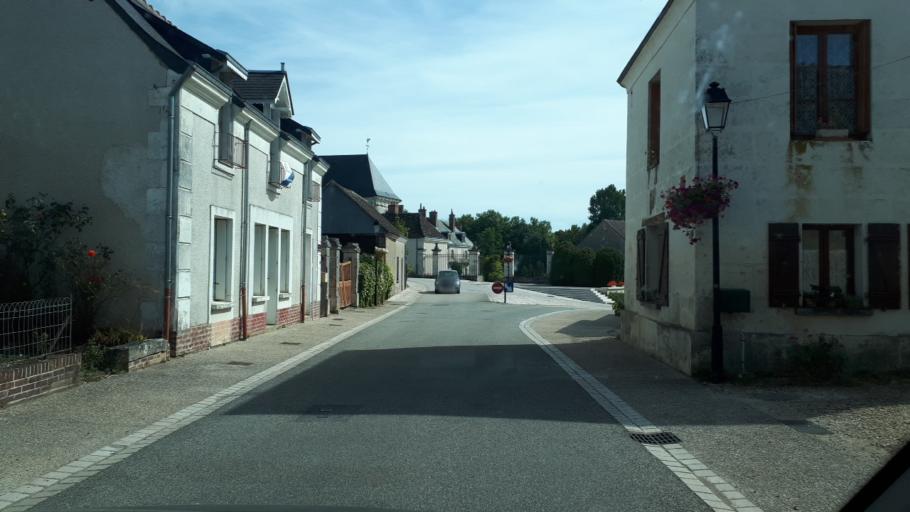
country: FR
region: Centre
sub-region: Departement du Loir-et-Cher
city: Montoire-sur-le-Loir
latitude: 47.7217
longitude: 0.8278
